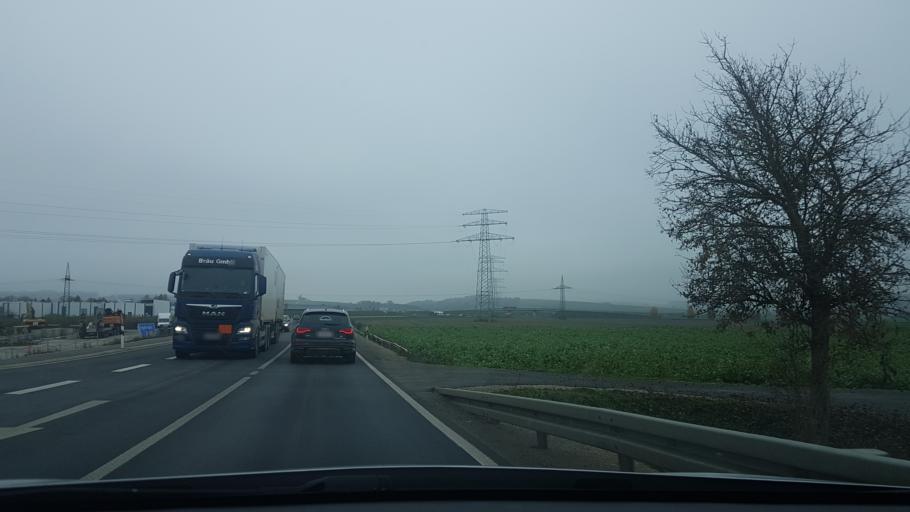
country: DE
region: Bavaria
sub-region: Lower Bavaria
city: Essenbach
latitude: 48.6047
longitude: 12.2333
